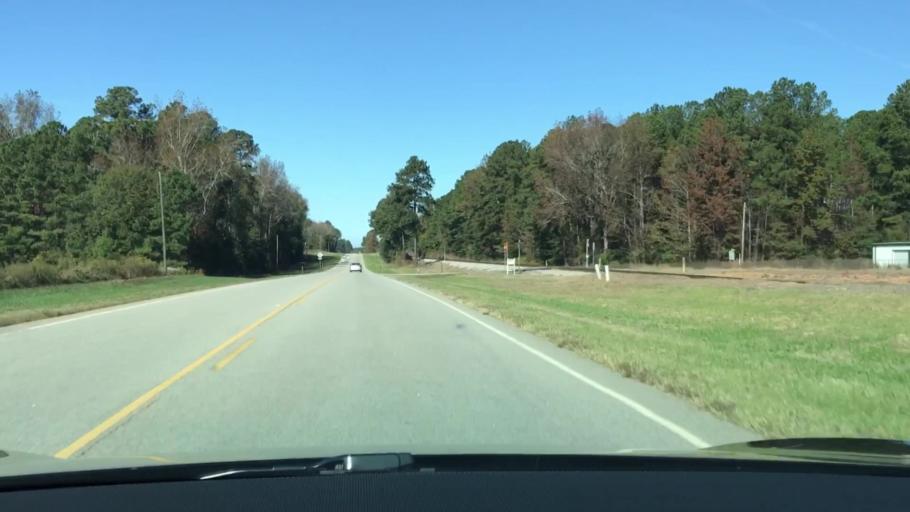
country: US
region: Georgia
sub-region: Warren County
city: Firing Range
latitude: 33.4679
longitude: -82.7157
